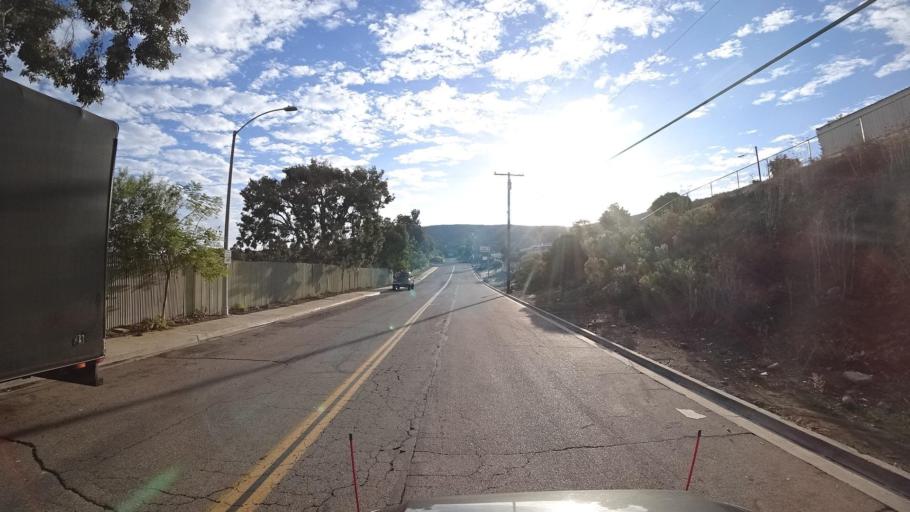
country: US
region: California
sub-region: San Diego County
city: La Presa
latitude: 32.7219
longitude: -116.9649
